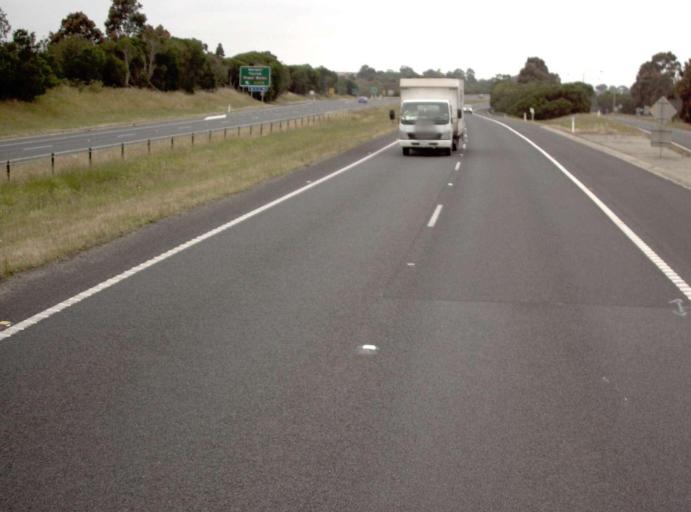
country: AU
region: Victoria
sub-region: Latrobe
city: Morwell
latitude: -38.2432
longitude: 146.4030
